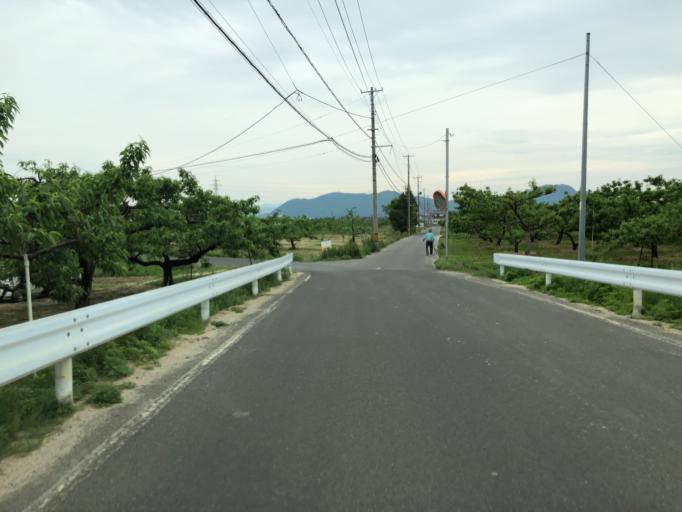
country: JP
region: Fukushima
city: Fukushima-shi
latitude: 37.8005
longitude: 140.4482
